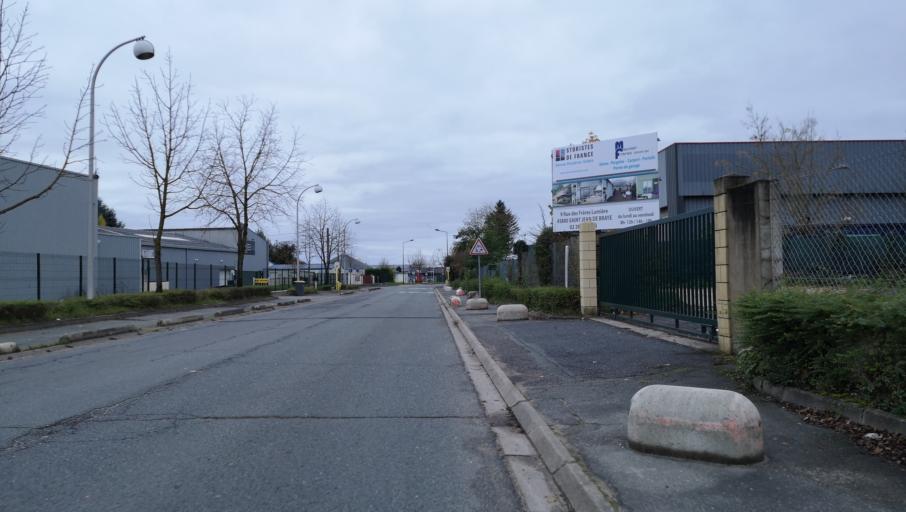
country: FR
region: Centre
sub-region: Departement du Loiret
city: Semoy
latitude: 47.9182
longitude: 1.9466
